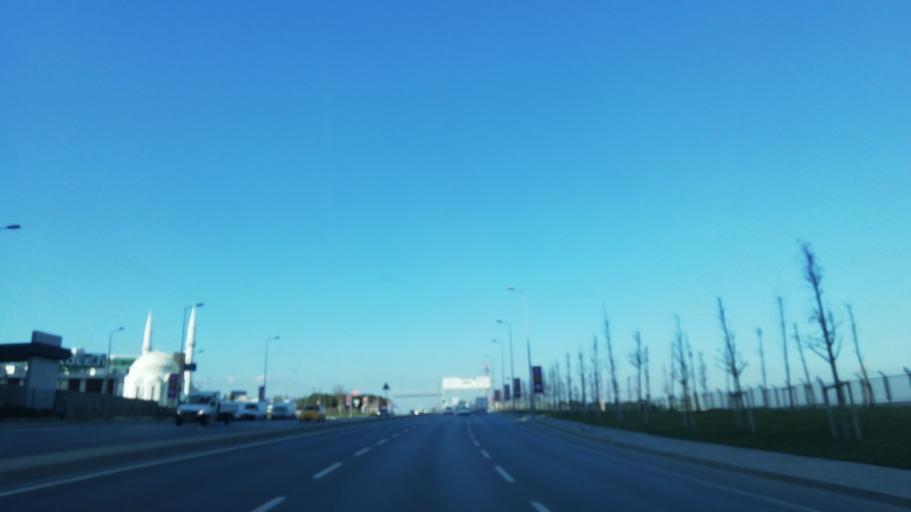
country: TR
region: Istanbul
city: Mahmutbey
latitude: 41.0660
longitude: 28.8398
